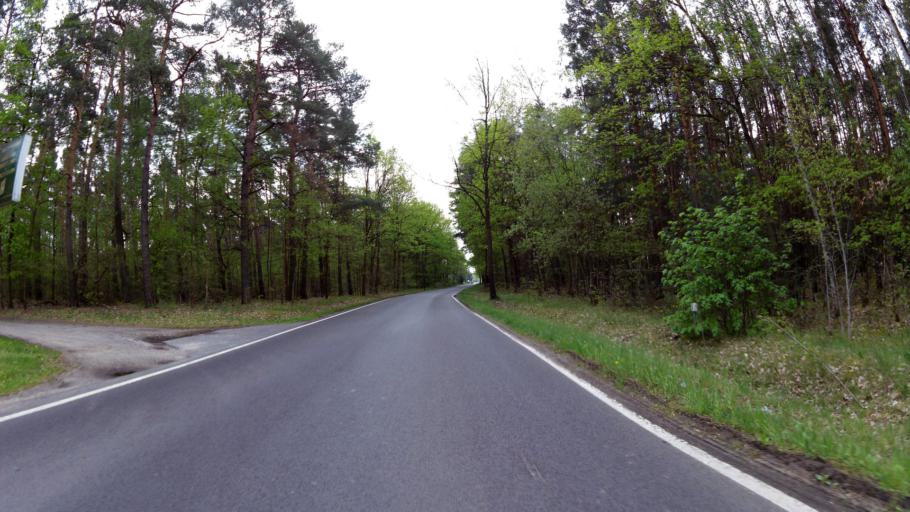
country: DE
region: Brandenburg
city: Bestensee
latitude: 52.2628
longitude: 13.7336
